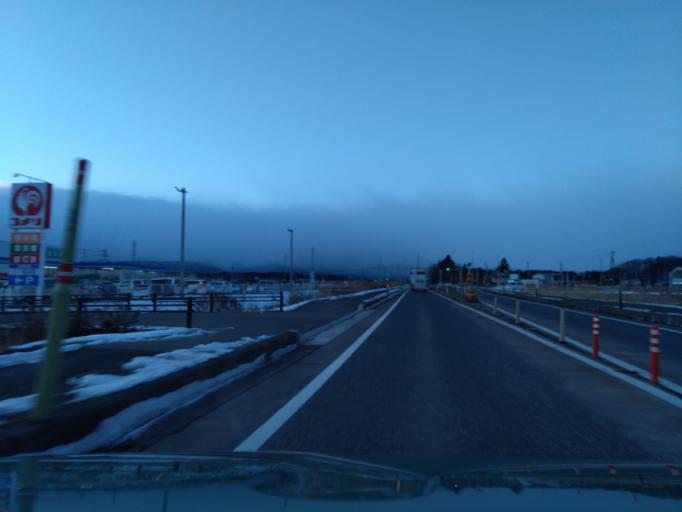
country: JP
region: Iwate
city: Shizukuishi
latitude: 39.6973
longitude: 140.9781
